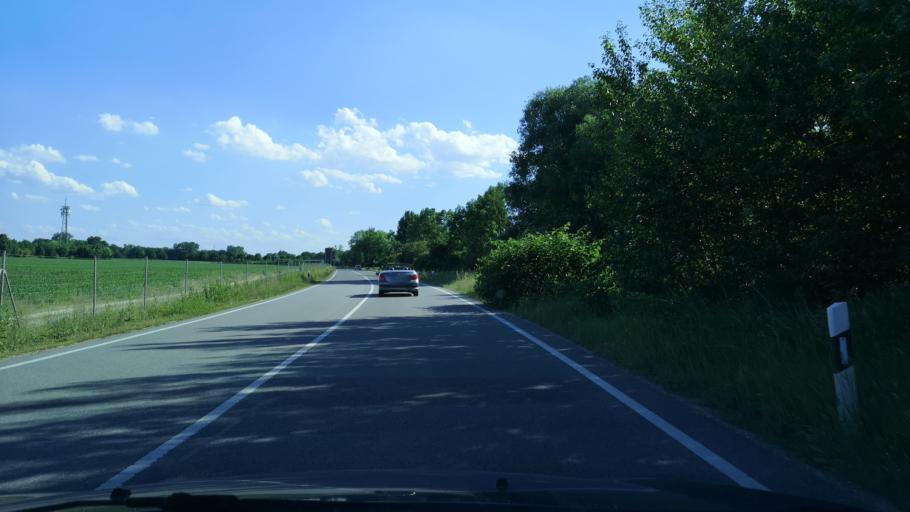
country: DE
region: Bavaria
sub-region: Upper Bavaria
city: Hallbergmoos
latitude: 48.3054
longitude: 11.7135
